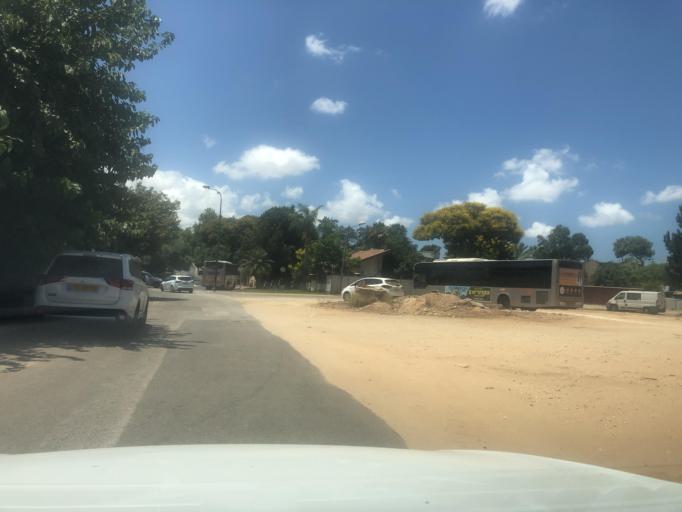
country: IL
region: Central District
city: Kfar Saba
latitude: 32.1588
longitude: 34.9164
